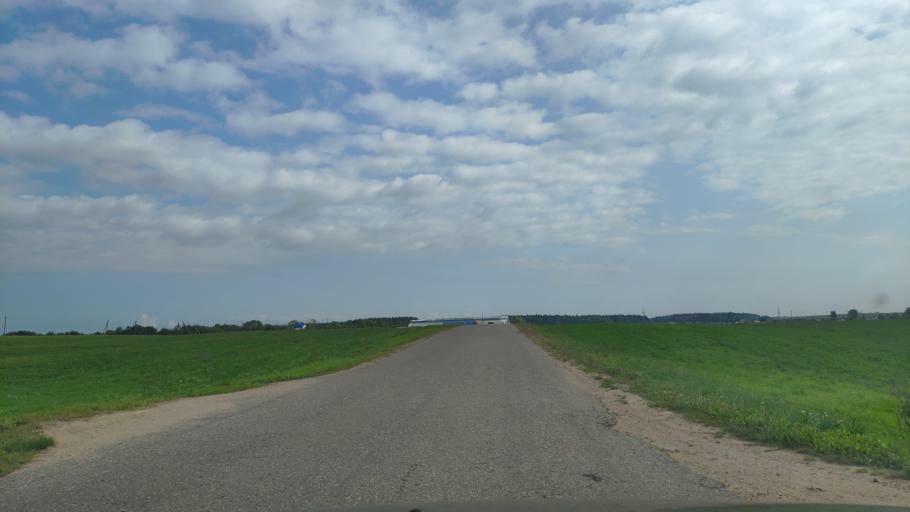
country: BY
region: Minsk
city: Khatsyezhyna
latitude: 53.8586
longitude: 27.3088
